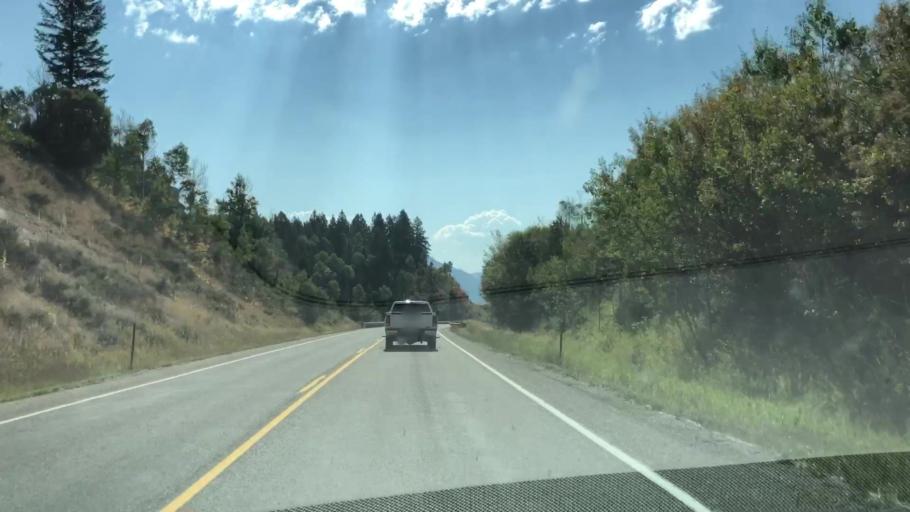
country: US
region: Wyoming
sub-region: Teton County
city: Hoback
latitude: 43.2306
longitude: -111.0902
